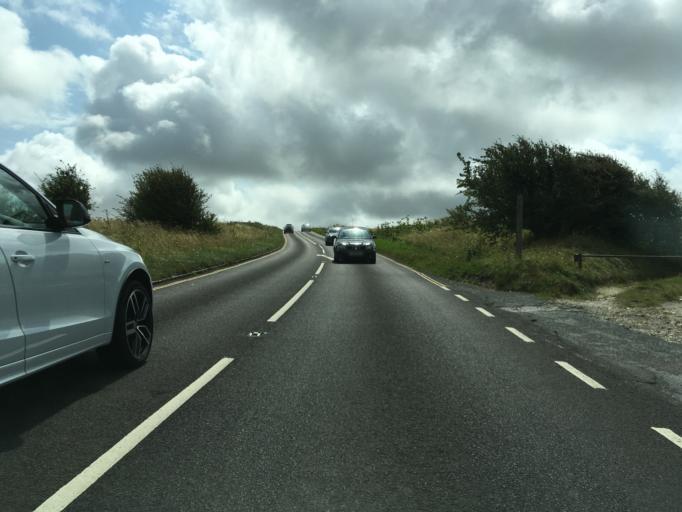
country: GB
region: England
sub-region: Brighton and Hove
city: Rottingdean
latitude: 50.8544
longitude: -0.0764
